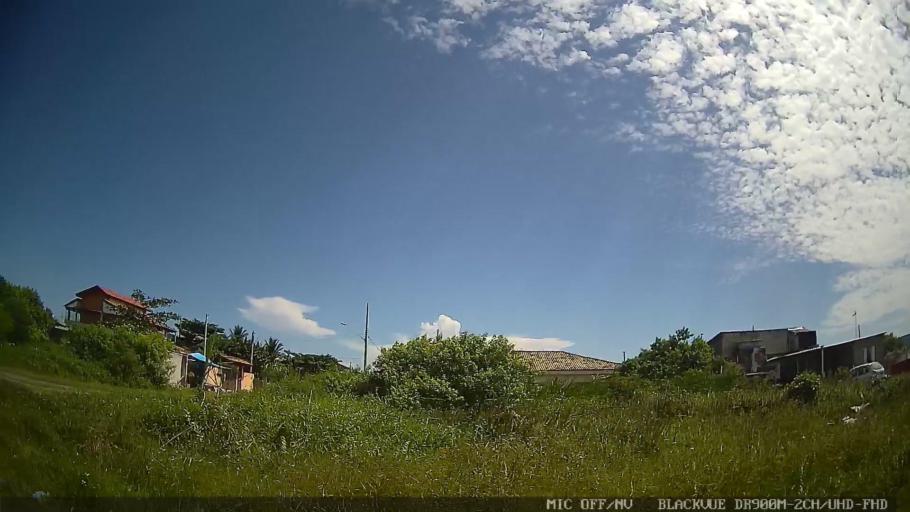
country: BR
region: Sao Paulo
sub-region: Iguape
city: Iguape
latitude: -24.7256
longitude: -47.5129
